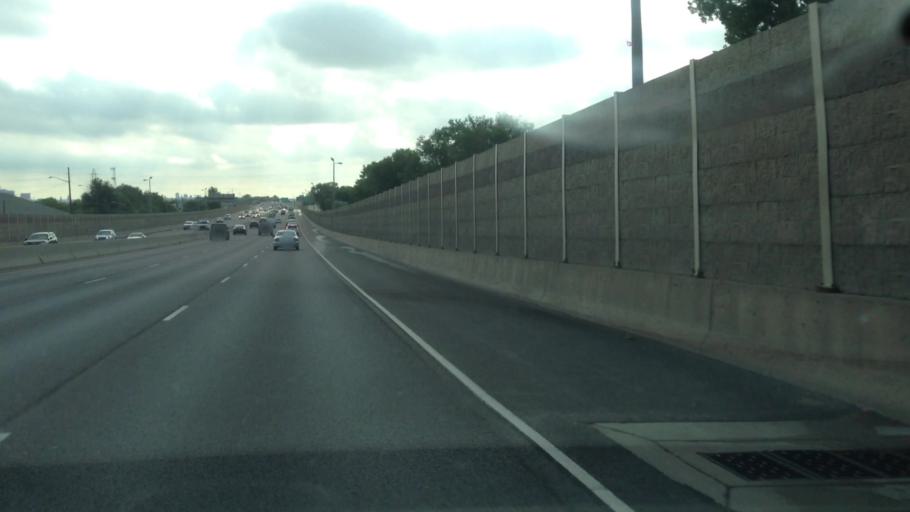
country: US
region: Colorado
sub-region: Jefferson County
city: Lakewood
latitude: 39.7248
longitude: -105.0677
